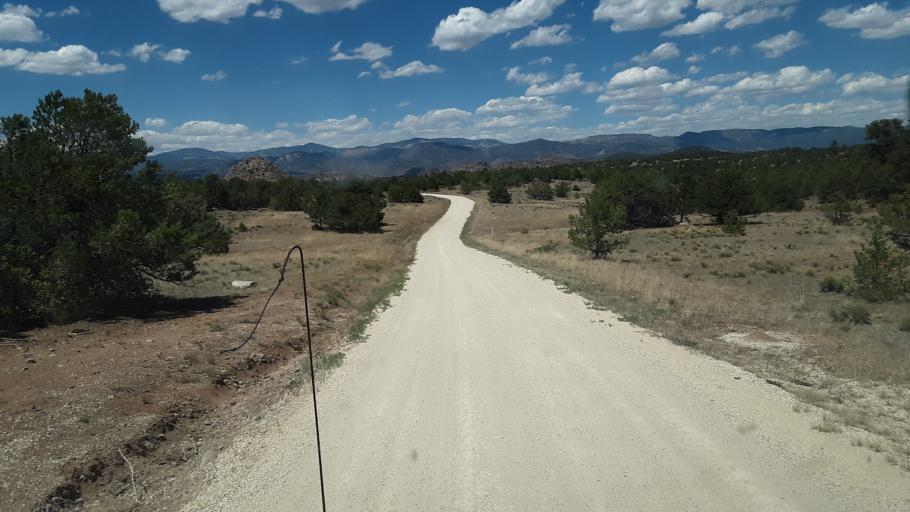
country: US
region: Colorado
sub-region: Custer County
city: Westcliffe
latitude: 38.3198
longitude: -105.6248
